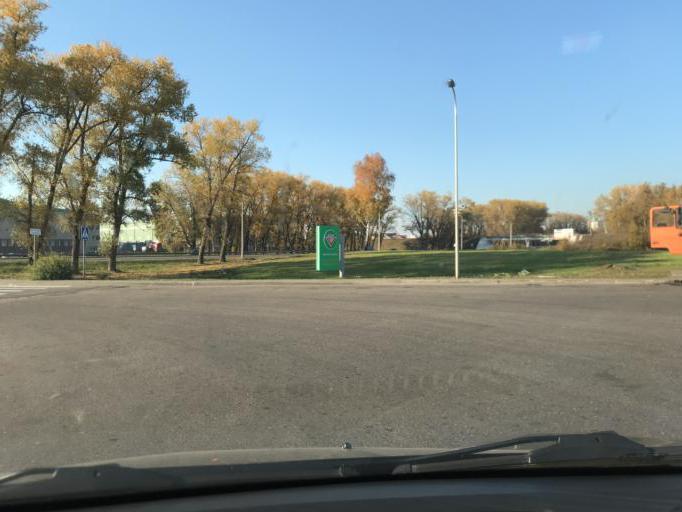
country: BY
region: Minsk
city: Yubilyeyny
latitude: 53.8119
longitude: 27.5313
